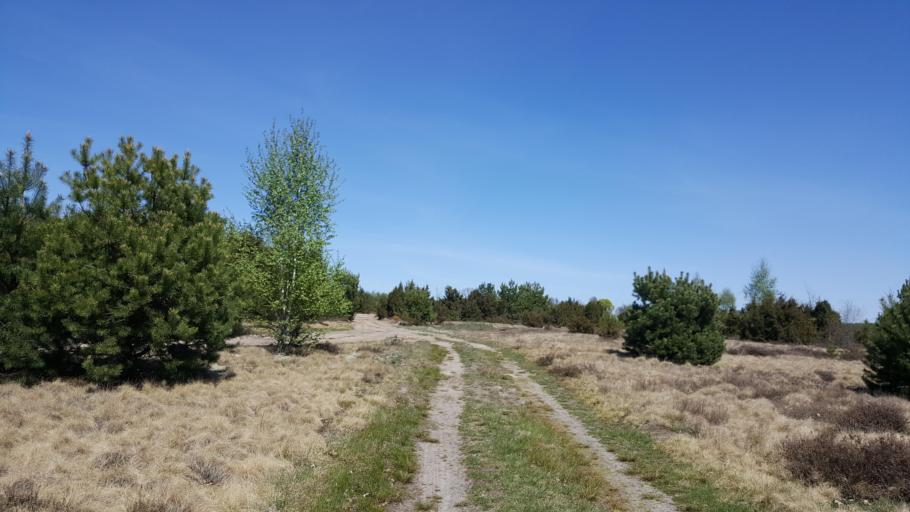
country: BY
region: Brest
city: Kamyanyets
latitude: 52.4206
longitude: 23.8369
